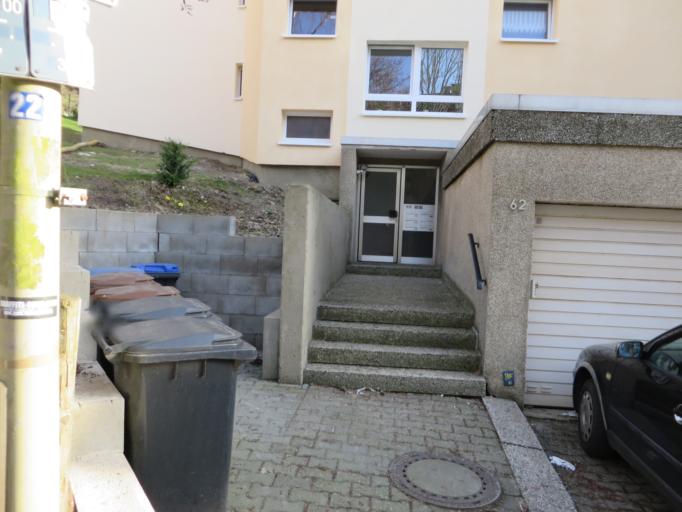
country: DE
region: North Rhine-Westphalia
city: Witten
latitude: 51.4343
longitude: 7.3462
